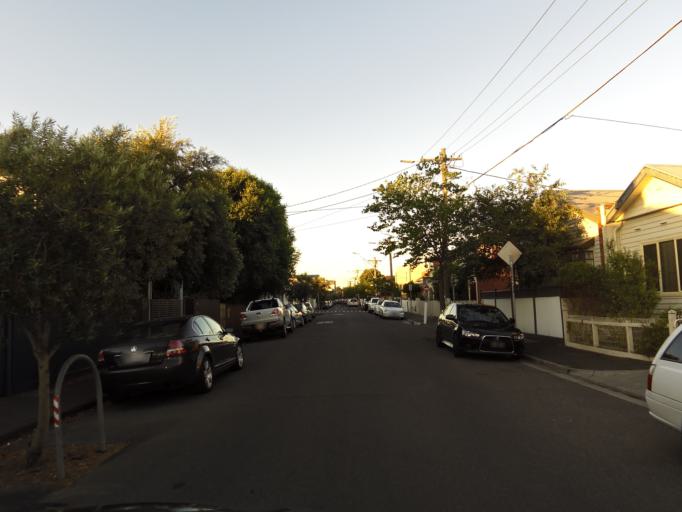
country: AU
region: Victoria
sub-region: Yarra
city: Richmond
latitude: -37.8234
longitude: 145.0044
